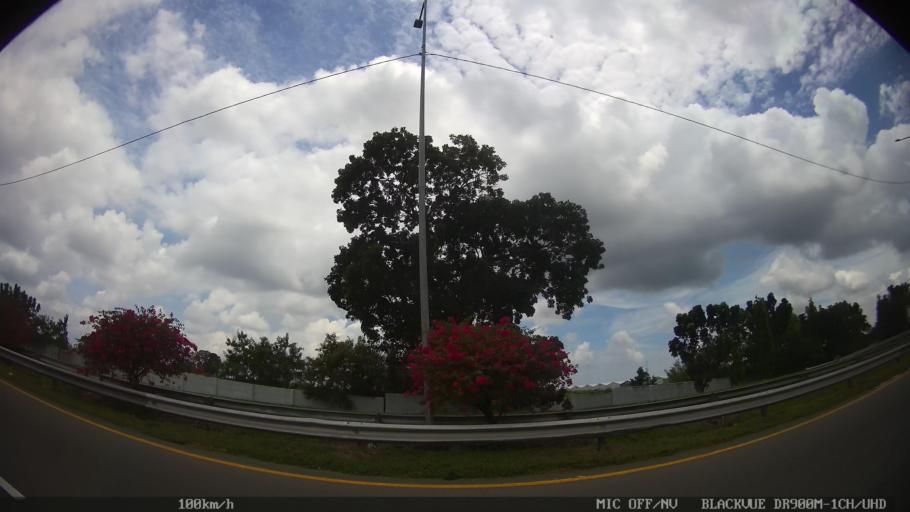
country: ID
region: North Sumatra
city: Medan
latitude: 3.6341
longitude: 98.7126
